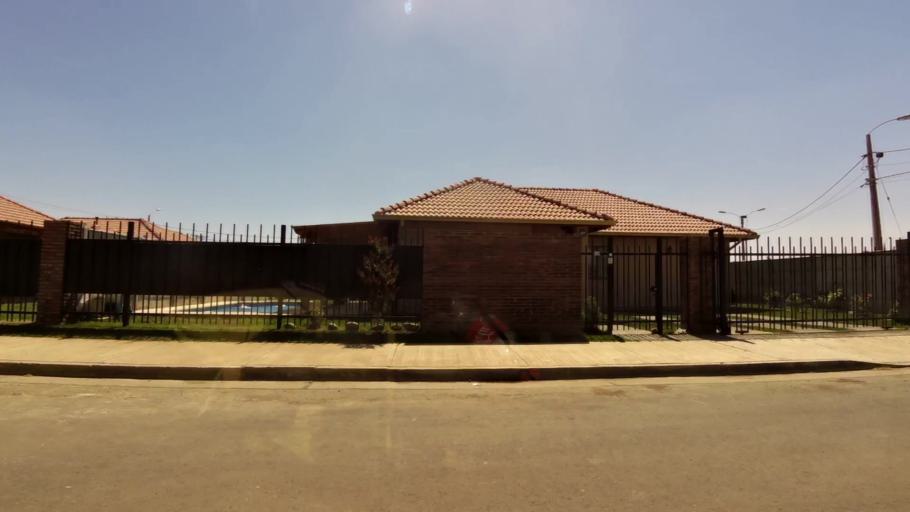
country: CL
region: Maule
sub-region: Provincia de Talca
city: Talca
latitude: -35.4351
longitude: -71.5924
